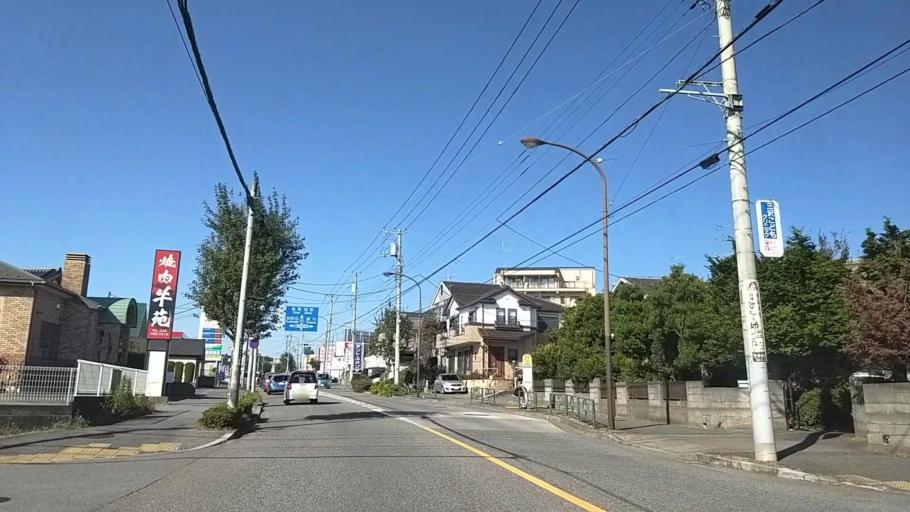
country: JP
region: Tokyo
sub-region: Machida-shi
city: Machida
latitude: 35.5779
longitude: 139.4124
